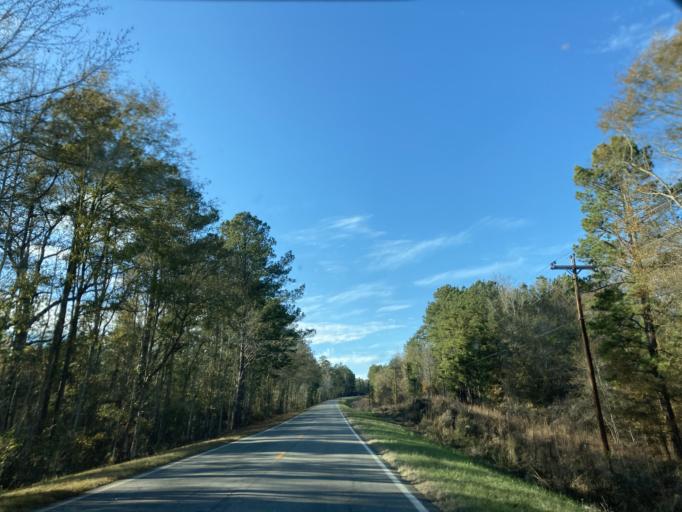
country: US
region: Georgia
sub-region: Jones County
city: Gray
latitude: 32.8883
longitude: -83.4999
